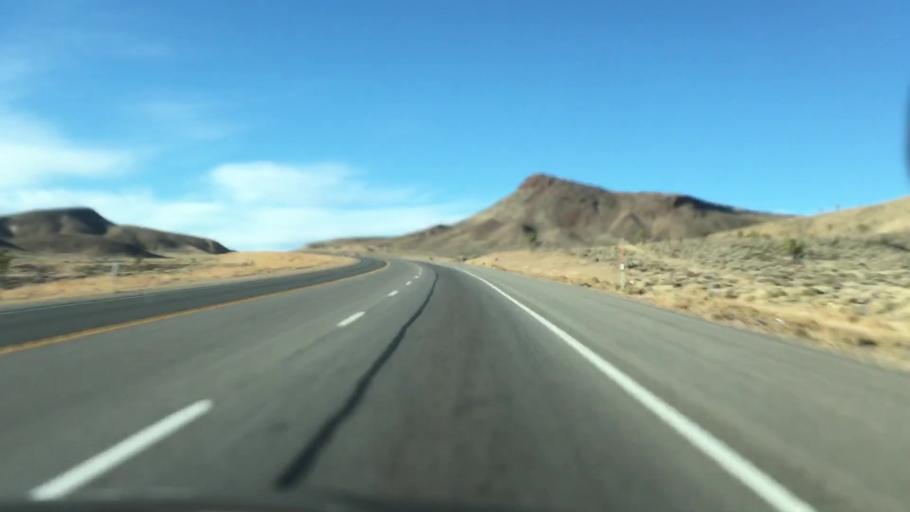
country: US
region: Nevada
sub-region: Esmeralda County
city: Goldfield
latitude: 37.6765
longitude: -117.2243
